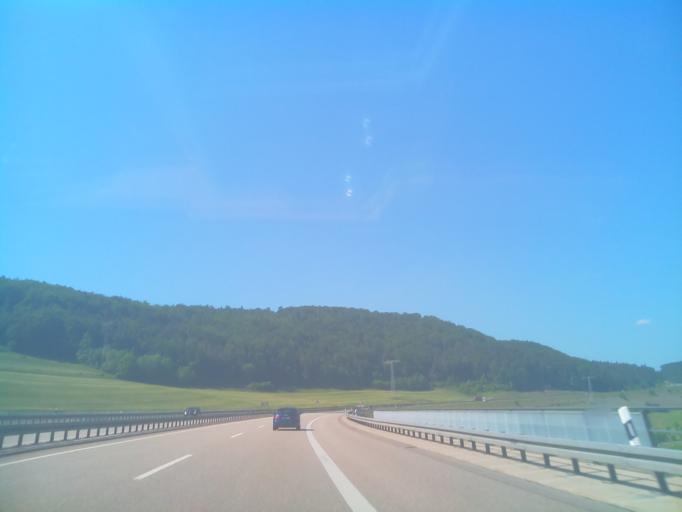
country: DE
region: Thuringia
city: Ellingshausen
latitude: 50.5529
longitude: 10.4749
